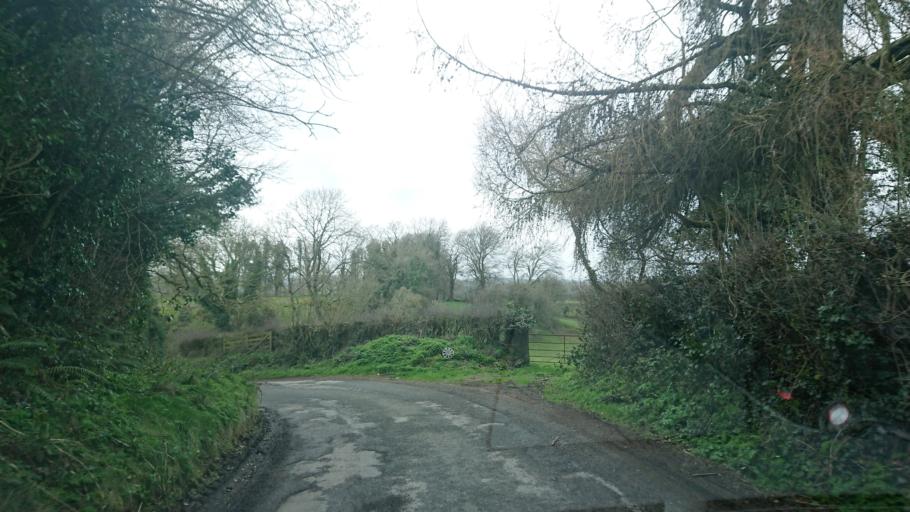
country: IE
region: Leinster
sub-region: Kildare
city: Eadestown
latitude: 53.1602
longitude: -6.5960
